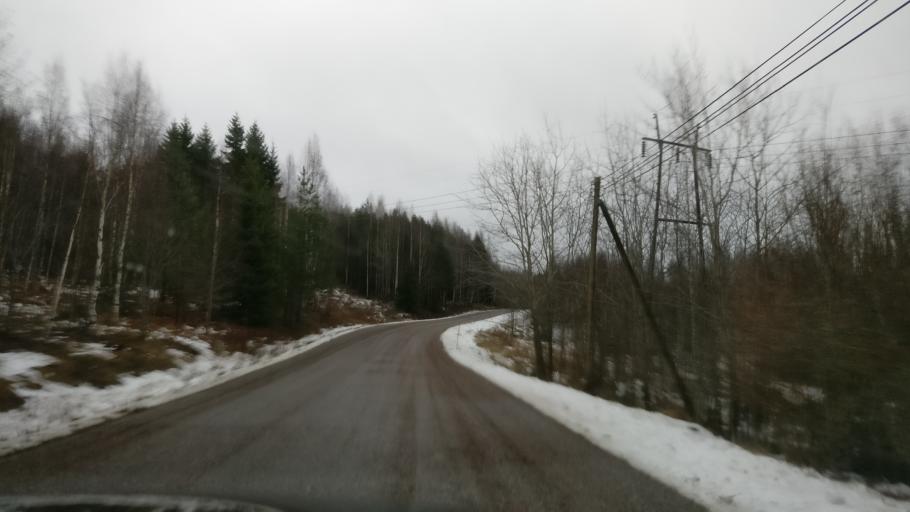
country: FI
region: Uusimaa
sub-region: Raaseporin
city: Karis
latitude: 60.0804
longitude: 23.7876
